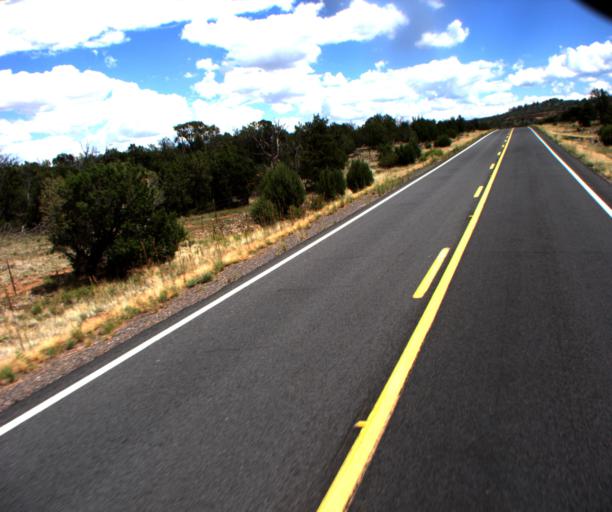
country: US
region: Arizona
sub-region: Coconino County
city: Parks
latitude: 35.5662
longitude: -111.9150
